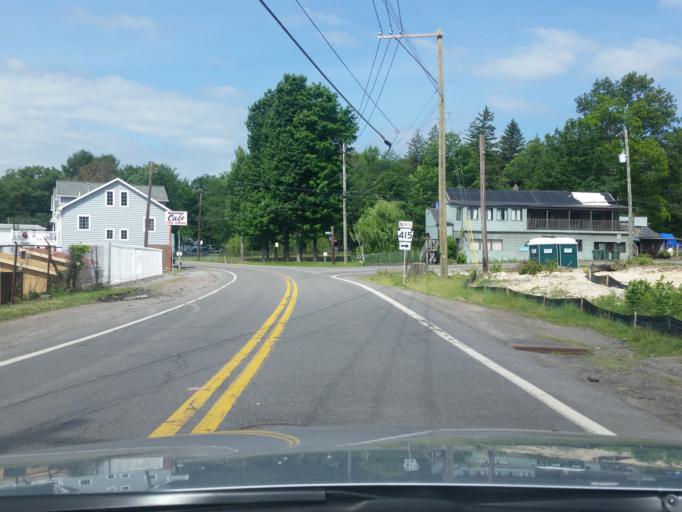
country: US
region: Pennsylvania
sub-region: Luzerne County
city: Harveys Lake
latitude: 41.3737
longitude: -76.0455
